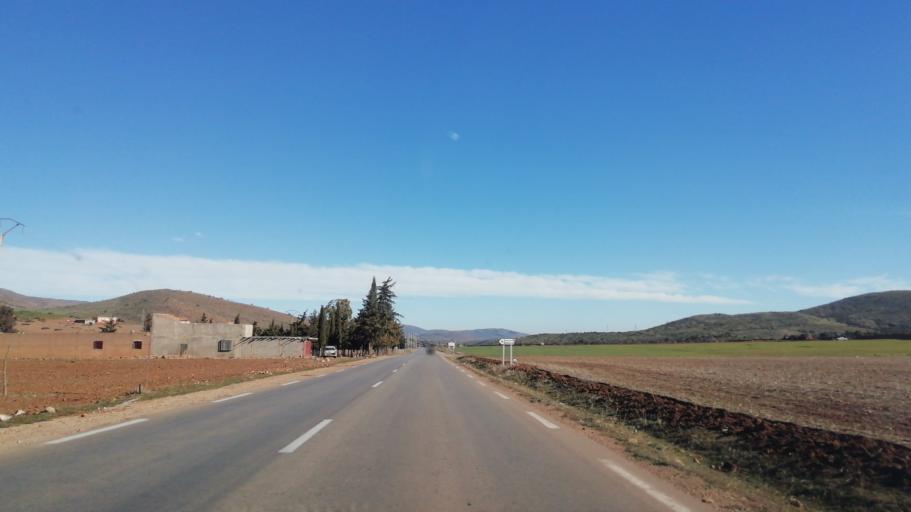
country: DZ
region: Tlemcen
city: Sebdou
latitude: 34.7408
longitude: -1.1690
